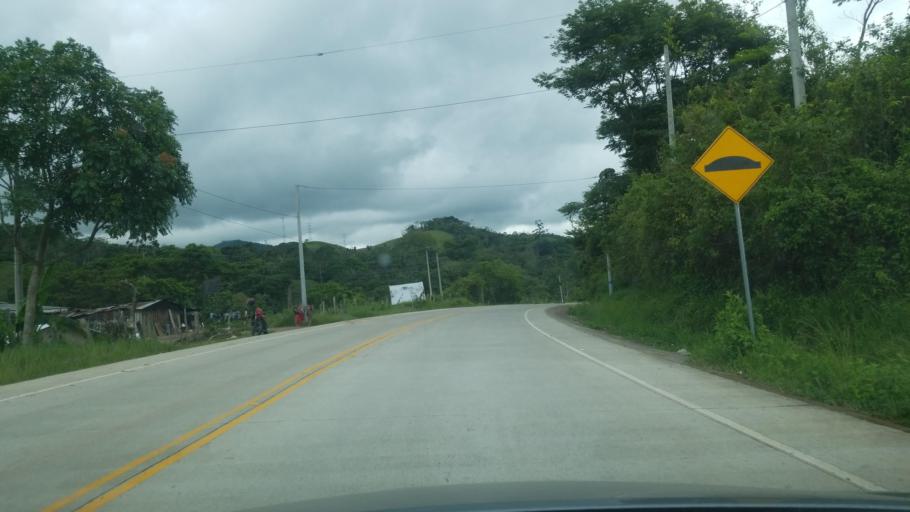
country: HN
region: Copan
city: San Jeronimo
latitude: 14.9356
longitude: -88.9212
